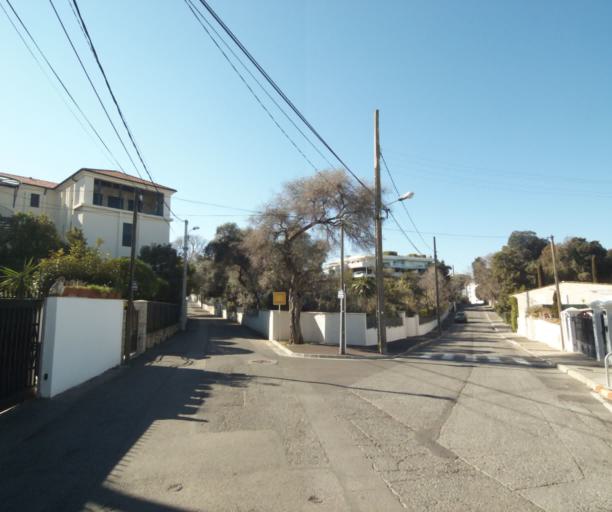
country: FR
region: Provence-Alpes-Cote d'Azur
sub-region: Departement des Alpes-Maritimes
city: Antibes
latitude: 43.5664
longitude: 7.1209
